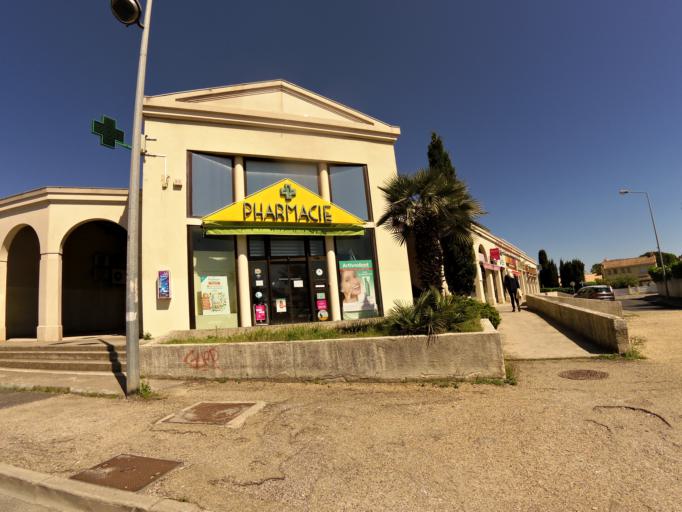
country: FR
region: Languedoc-Roussillon
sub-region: Departement de l'Herault
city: Castries
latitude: 43.6751
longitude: 3.9830
